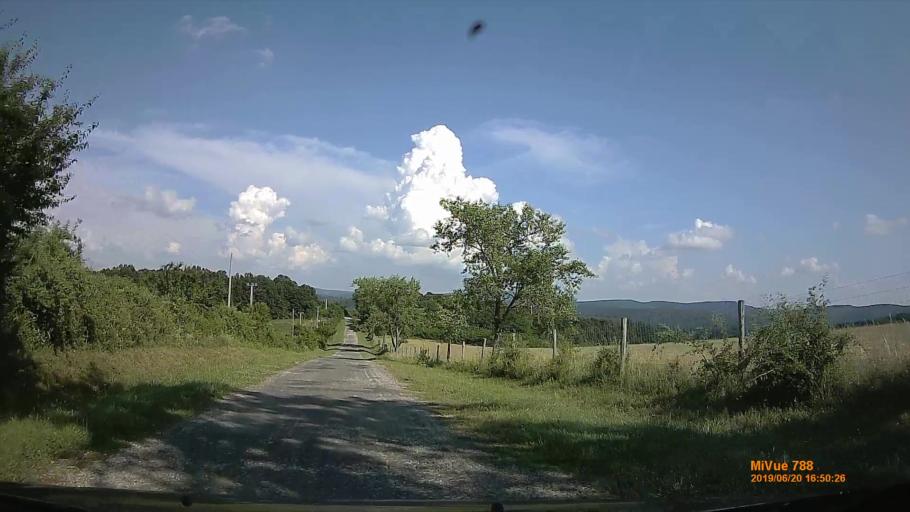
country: HU
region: Baranya
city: Buekkoesd
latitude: 46.1579
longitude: 18.0441
